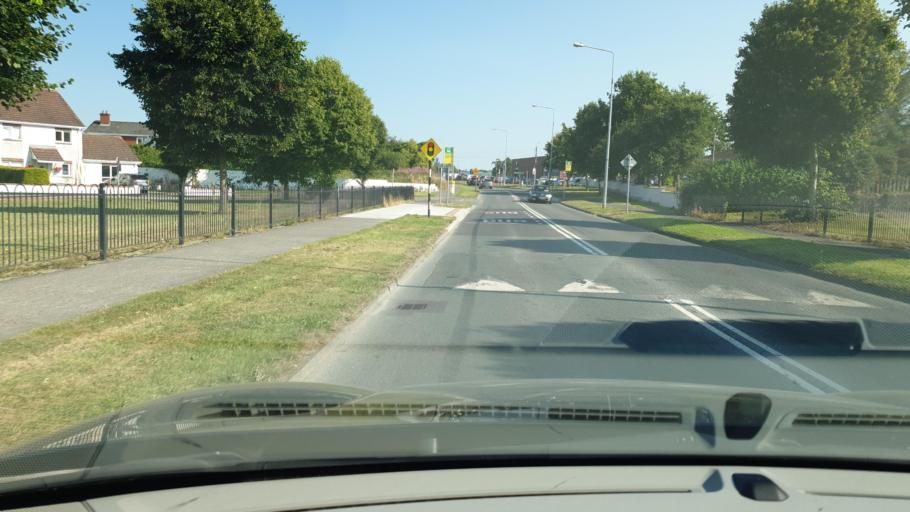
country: IE
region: Leinster
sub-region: An Mhi
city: Navan
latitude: 53.6473
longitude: -6.7001
